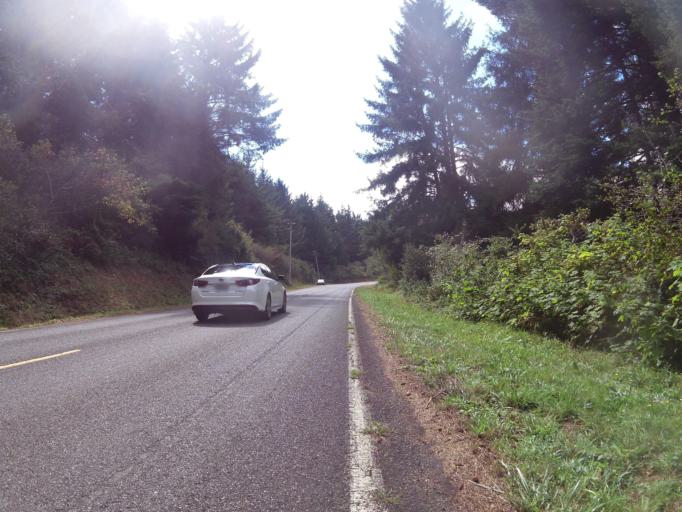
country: US
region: California
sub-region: Humboldt County
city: Humboldt Hill
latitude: 40.6580
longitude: -124.2099
